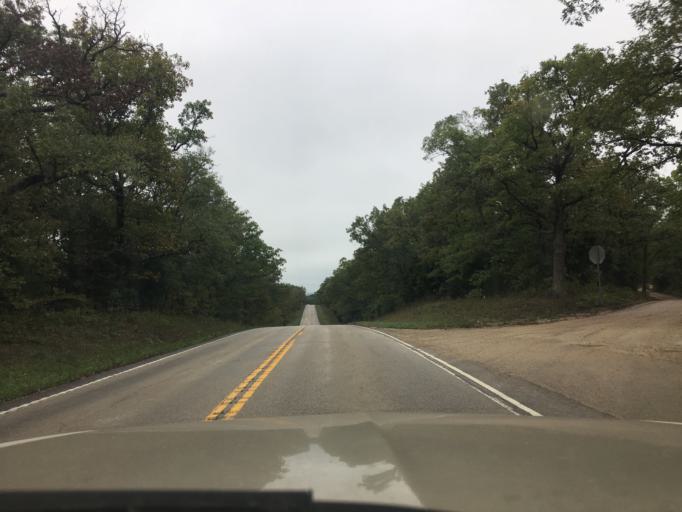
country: US
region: Missouri
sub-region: Crawford County
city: Cuba
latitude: 38.2043
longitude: -91.4433
